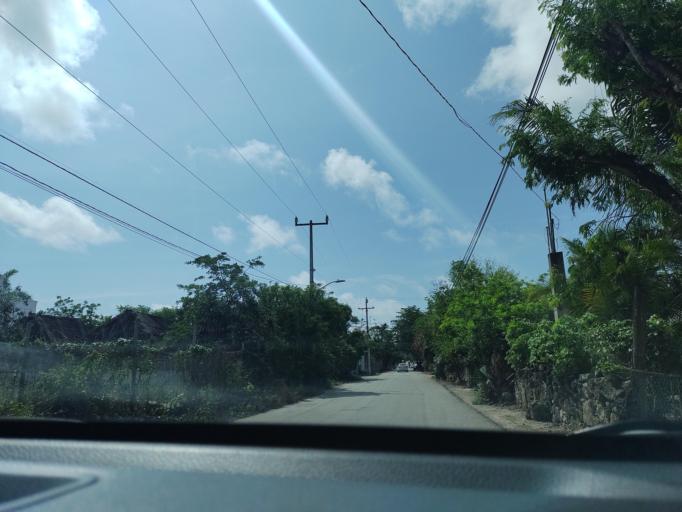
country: MX
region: Quintana Roo
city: Tulum
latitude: 20.2120
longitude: -87.4711
